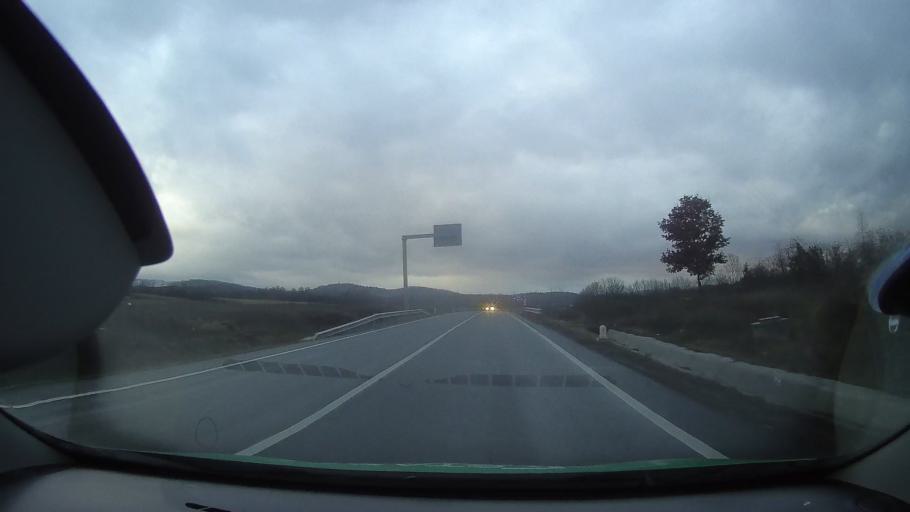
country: RO
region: Hunedoara
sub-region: Comuna Baia de Cris
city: Baia de Cris
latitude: 46.1705
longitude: 22.7199
